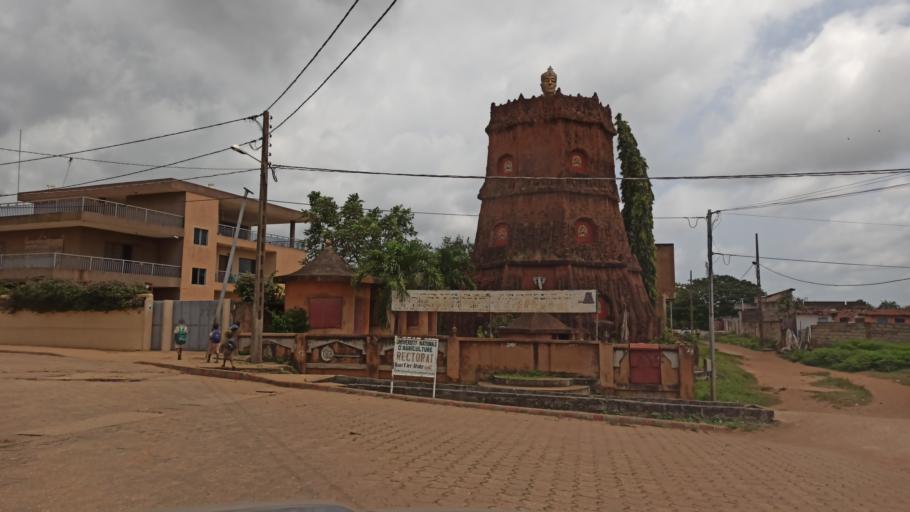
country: BJ
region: Queme
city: Porto-Novo
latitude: 6.4690
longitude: 2.6326
